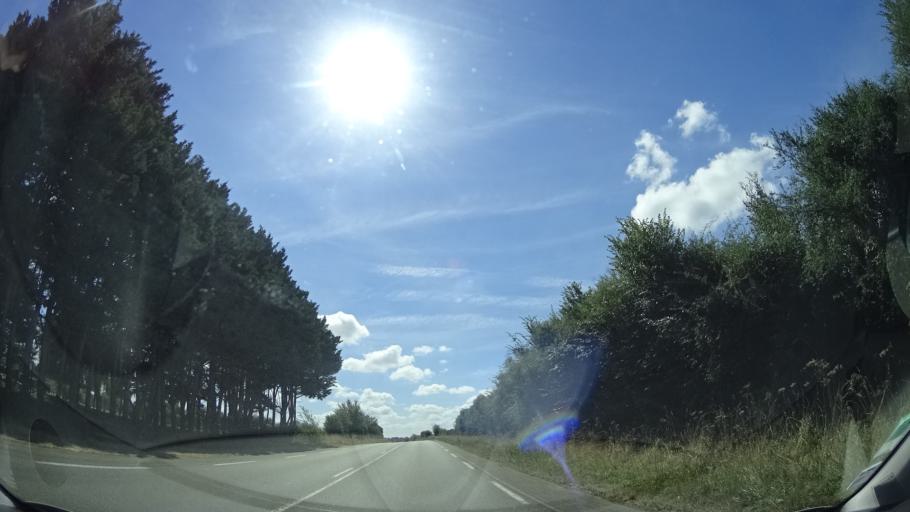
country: FR
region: Pays de la Loire
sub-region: Departement de la Sarthe
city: Auvers-le-Hamon
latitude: 47.8847
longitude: -0.4090
